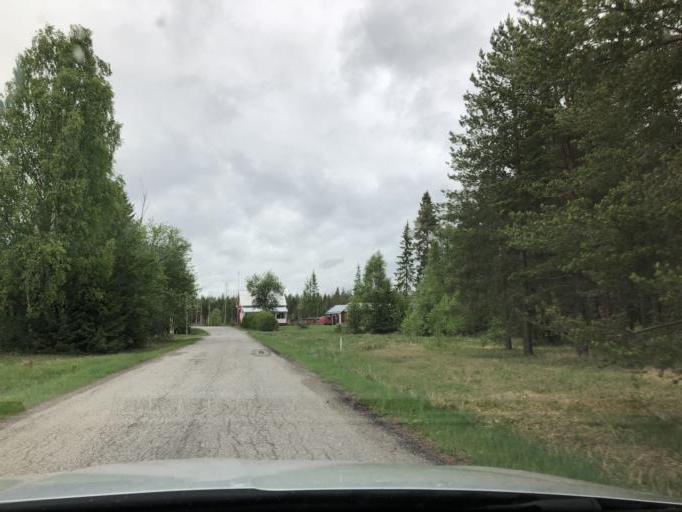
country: SE
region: Norrbotten
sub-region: Pitea Kommun
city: Roknas
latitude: 65.3774
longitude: 21.2783
